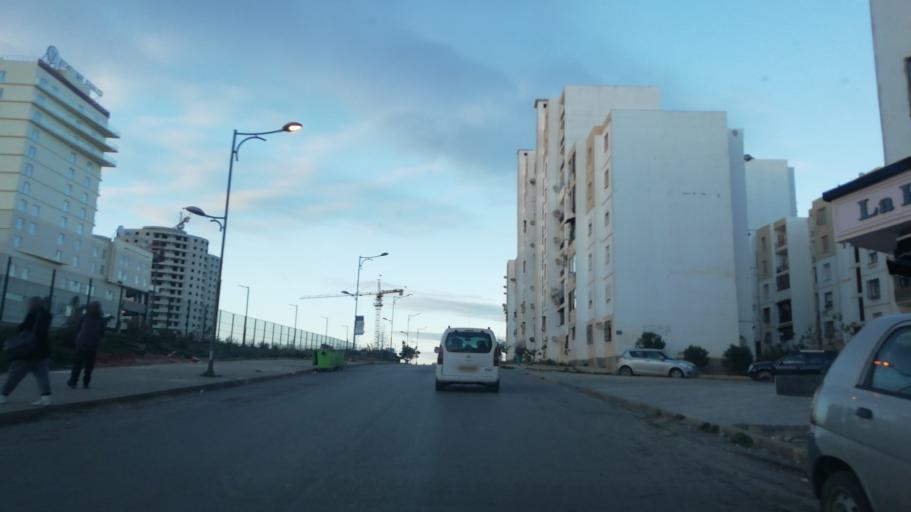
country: DZ
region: Oran
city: Bir el Djir
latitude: 35.7056
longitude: -0.5603
